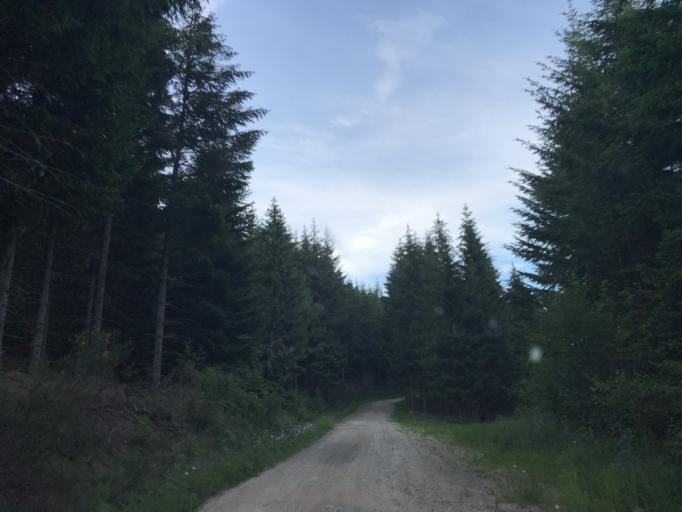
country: FR
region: Rhone-Alpes
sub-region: Departement de la Loire
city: Noiretable
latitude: 45.8070
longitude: 3.7046
